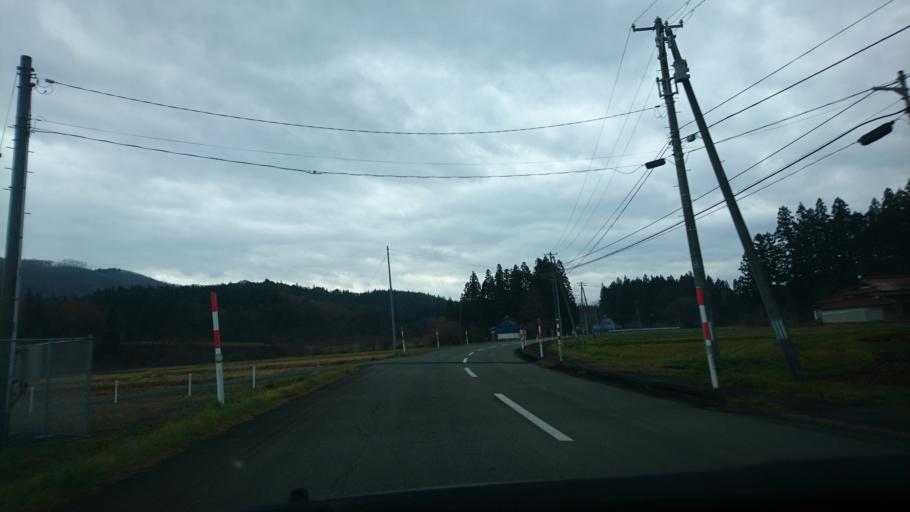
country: JP
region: Iwate
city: Ichinoseki
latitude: 38.9573
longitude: 140.9399
